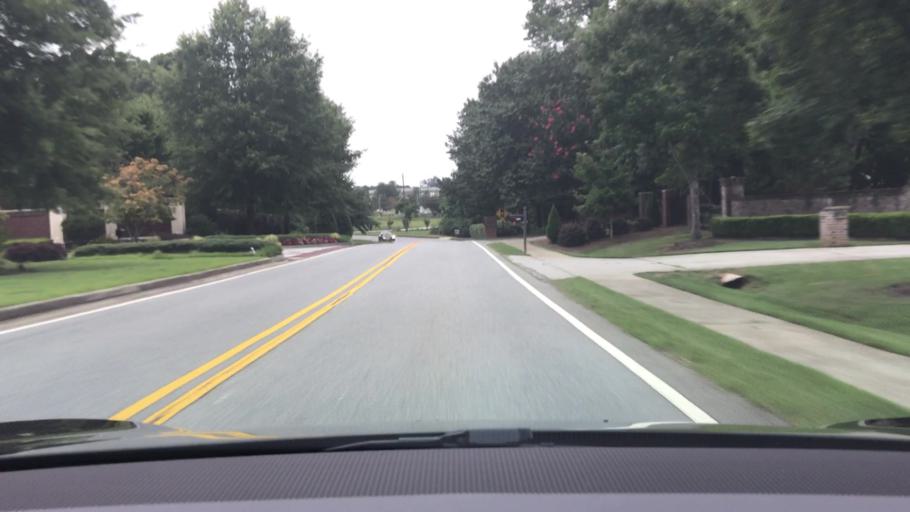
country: US
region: Georgia
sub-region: Gwinnett County
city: Suwanee
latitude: 34.0825
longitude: -84.0759
